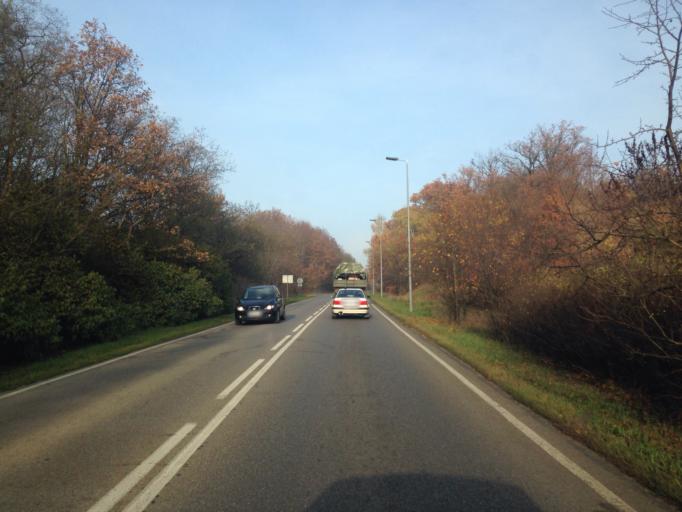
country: PL
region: Kujawsko-Pomorskie
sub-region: Powiat bydgoski
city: Osielsko
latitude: 53.1670
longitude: 18.0456
